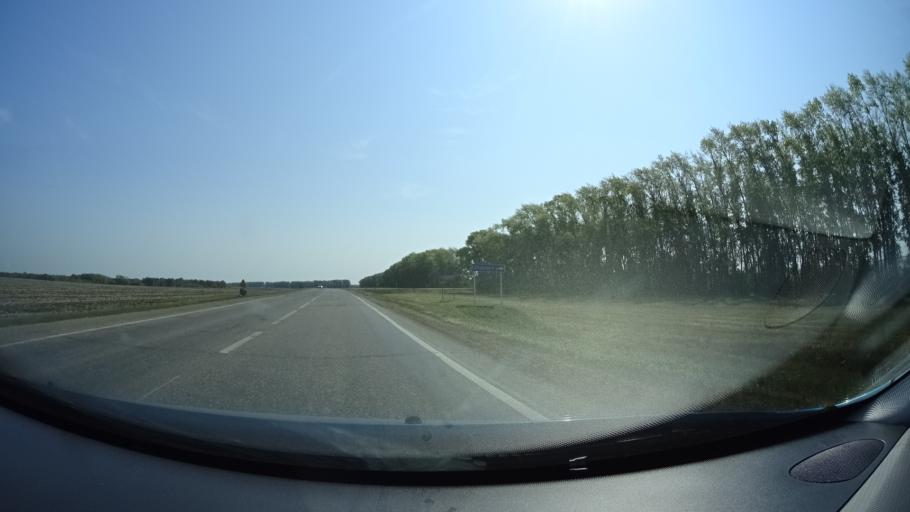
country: RU
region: Bashkortostan
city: Karmaskaly
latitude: 54.3899
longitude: 56.1253
